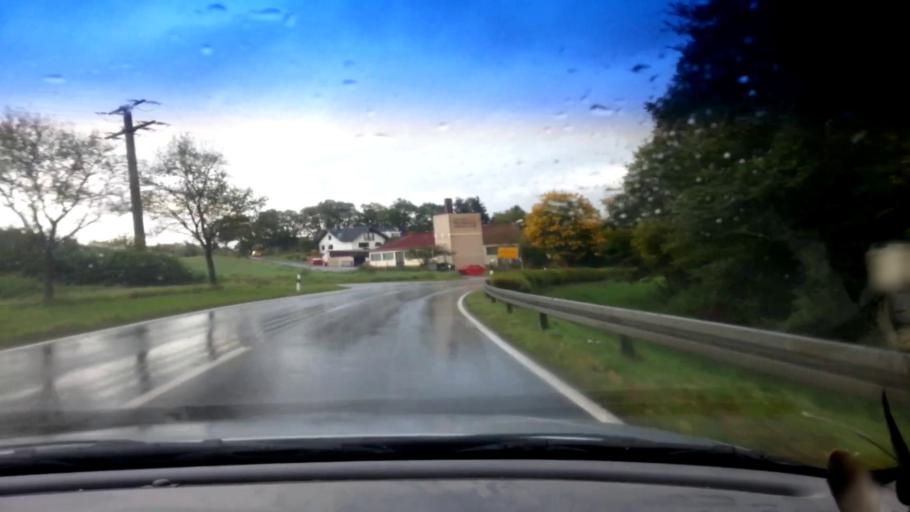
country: DE
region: Bavaria
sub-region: Upper Franconia
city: Burgebrach
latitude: 49.8348
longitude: 10.7409
